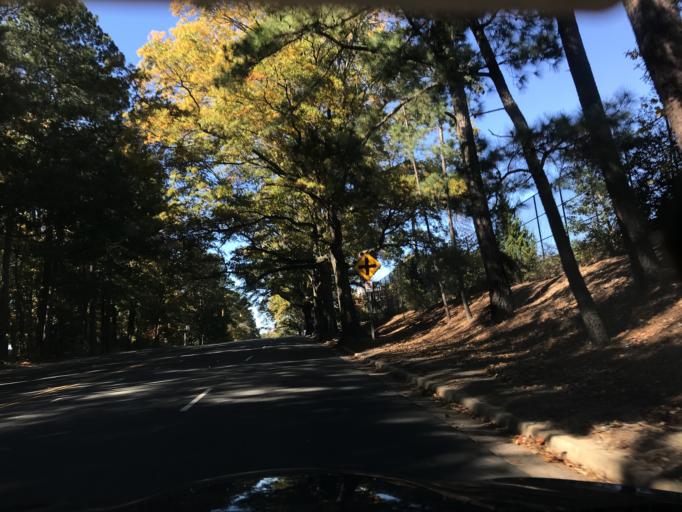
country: US
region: North Carolina
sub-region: Durham County
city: Durham
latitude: 35.9942
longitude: -78.9458
